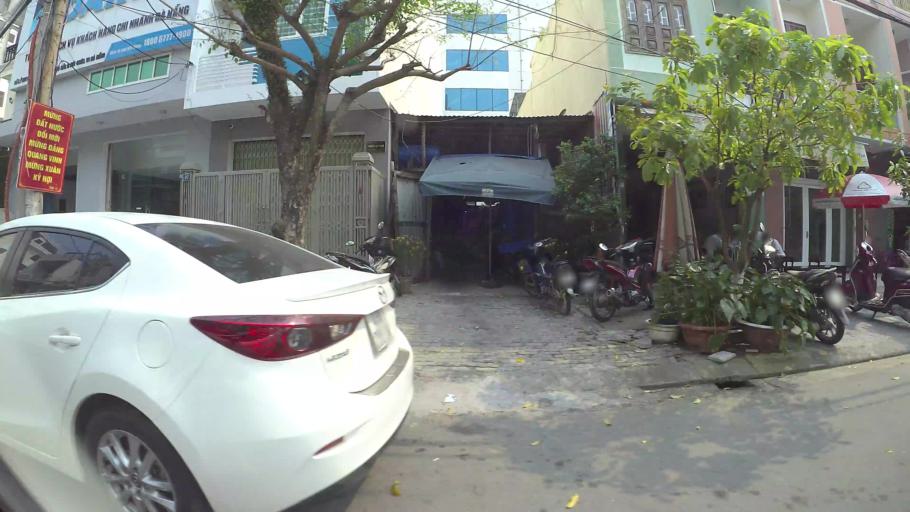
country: VN
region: Da Nang
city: Son Tra
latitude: 16.0414
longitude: 108.2204
